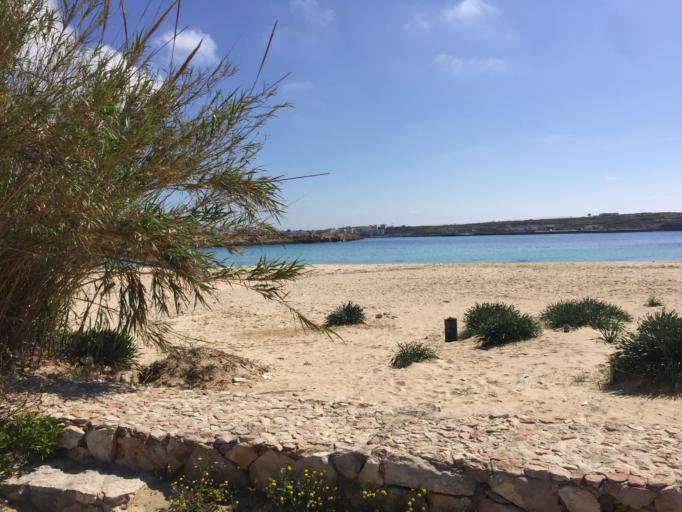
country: IT
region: Sicily
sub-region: Agrigento
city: Lampedusa
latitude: 35.4988
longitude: 12.5987
